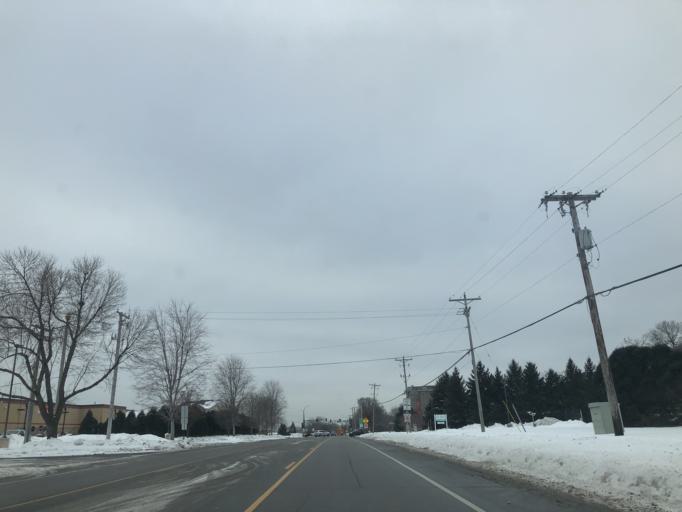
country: US
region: Minnesota
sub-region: Ramsey County
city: New Brighton
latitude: 45.0816
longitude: -93.1883
